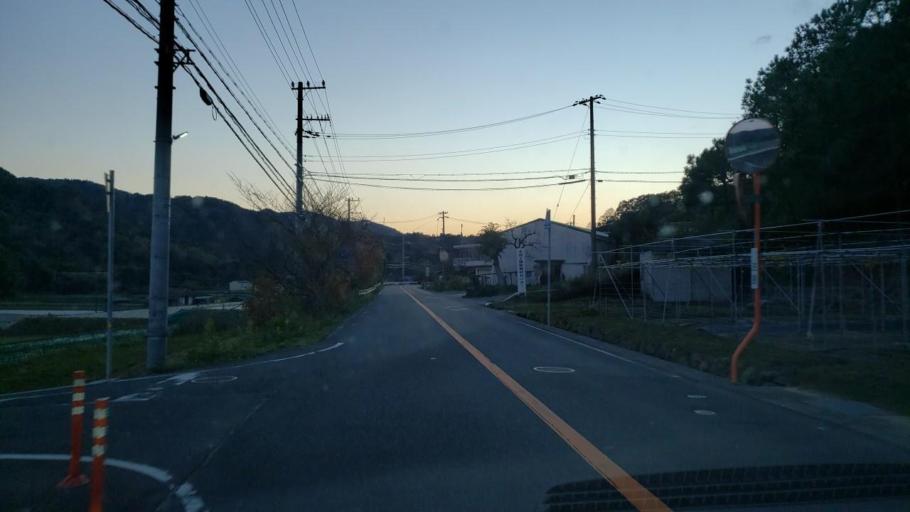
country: JP
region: Hyogo
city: Fukura
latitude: 34.2923
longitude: 134.7222
